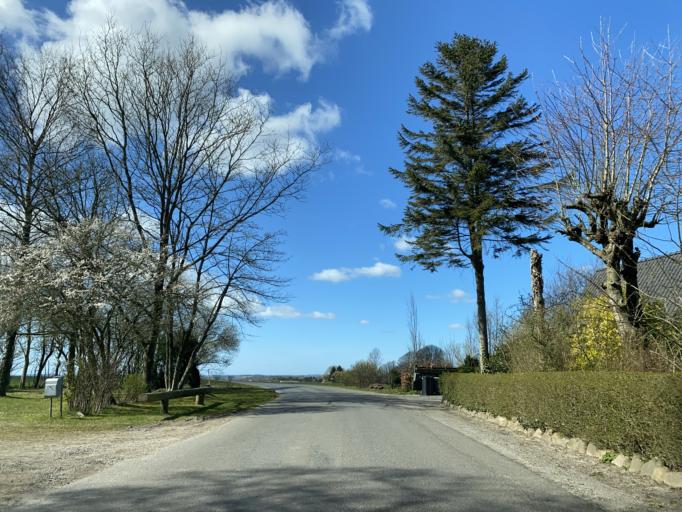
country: DK
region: Central Jutland
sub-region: Favrskov Kommune
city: Ulstrup
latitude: 56.3431
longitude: 9.8120
